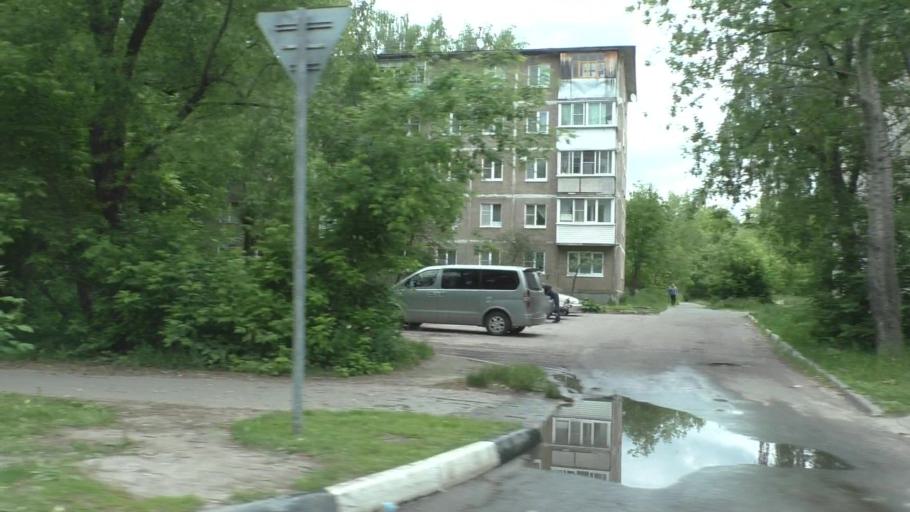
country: RU
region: Moskovskaya
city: Yegor'yevsk
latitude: 55.3687
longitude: 39.0540
